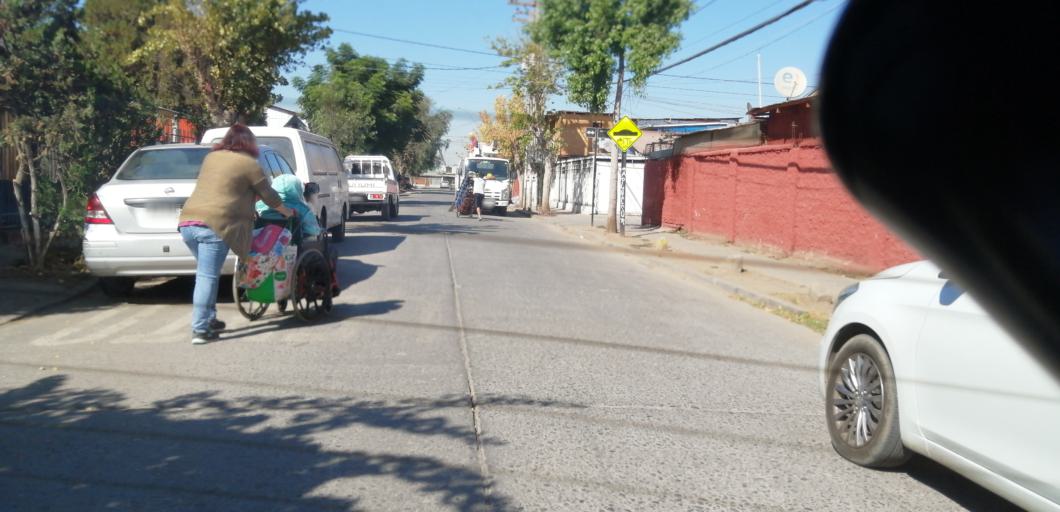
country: CL
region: Santiago Metropolitan
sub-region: Provincia de Santiago
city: Lo Prado
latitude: -33.4371
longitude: -70.7550
